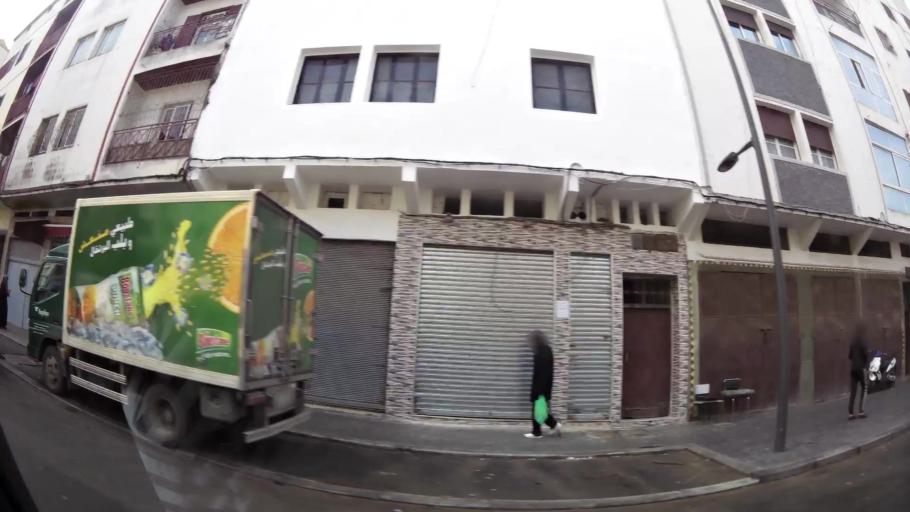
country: MA
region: Grand Casablanca
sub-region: Casablanca
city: Casablanca
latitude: 33.5725
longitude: -7.5829
